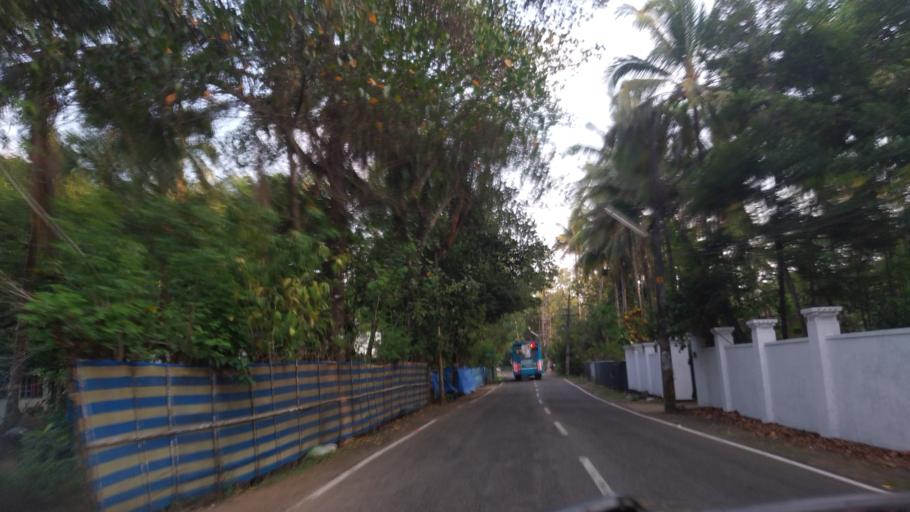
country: IN
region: Kerala
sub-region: Thrissur District
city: Thanniyam
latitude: 10.3711
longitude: 76.1049
